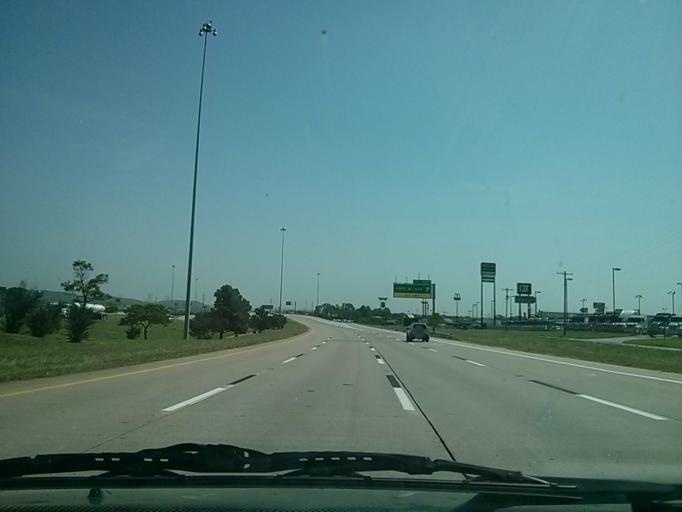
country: US
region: Oklahoma
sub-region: Tulsa County
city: Oakhurst
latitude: 36.0757
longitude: -96.0526
